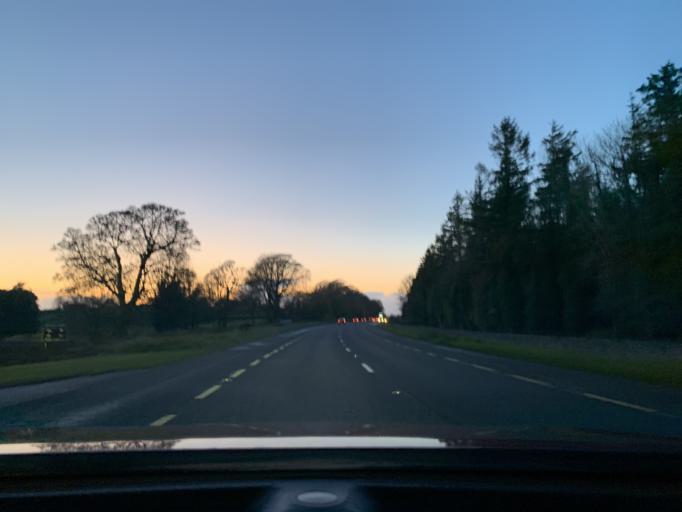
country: IE
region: Connaught
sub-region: Roscommon
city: Boyle
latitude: 53.9689
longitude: -8.2239
